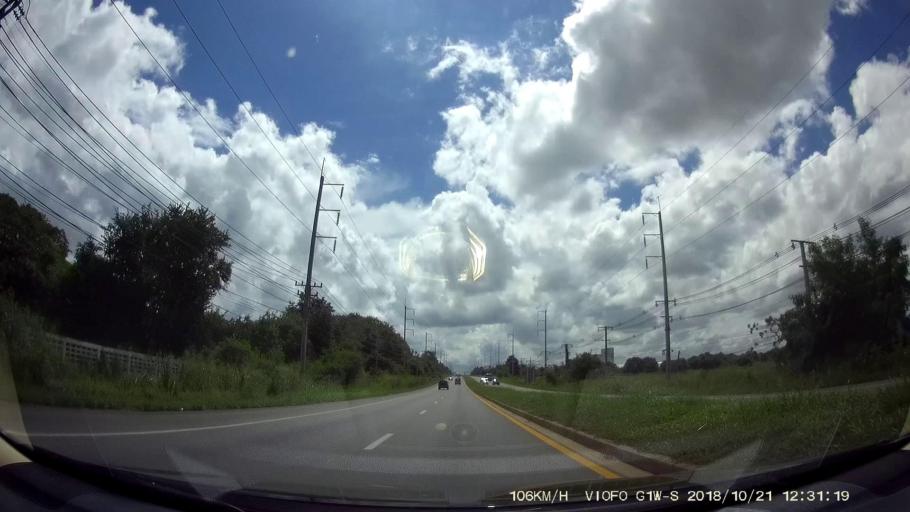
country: TH
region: Nakhon Ratchasima
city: Dan Khun Thot
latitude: 15.1583
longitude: 101.7354
